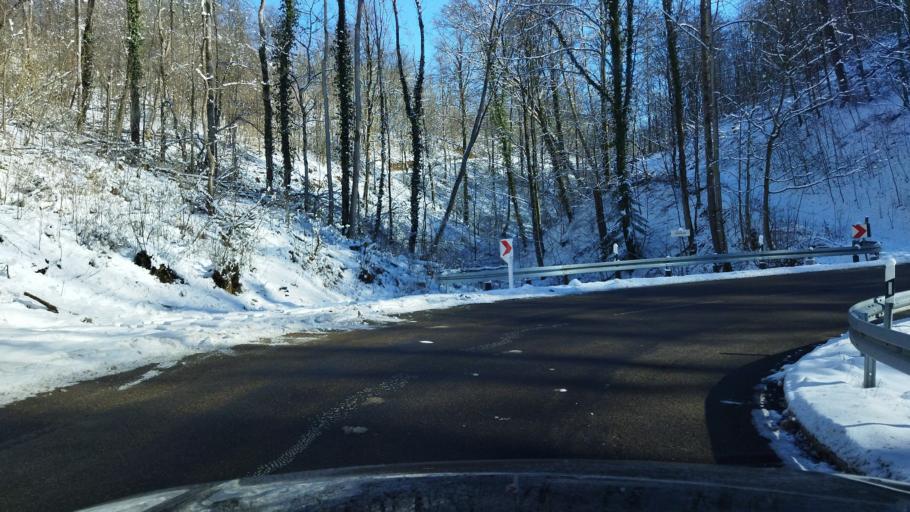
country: DE
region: Baden-Wuerttemberg
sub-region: Regierungsbezirk Stuttgart
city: Langenburg
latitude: 49.2571
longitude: 9.8555
